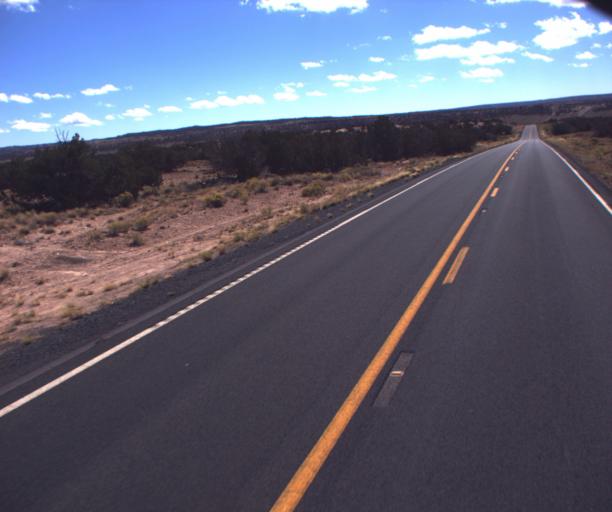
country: US
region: Arizona
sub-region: Apache County
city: Houck
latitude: 35.1073
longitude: -109.3167
